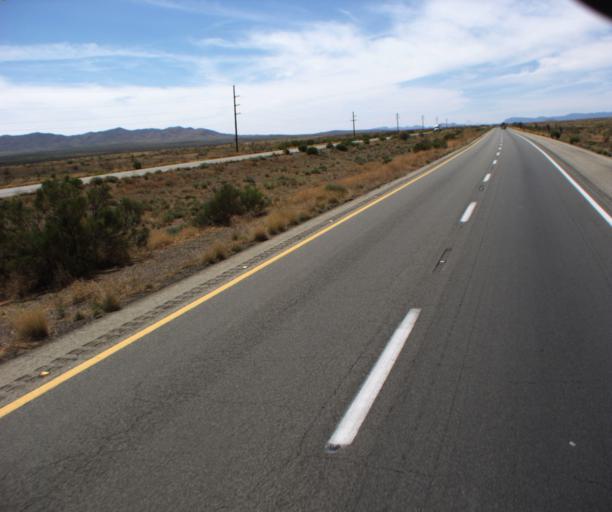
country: US
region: Arizona
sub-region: Cochise County
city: Willcox
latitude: 32.3626
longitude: -109.6493
